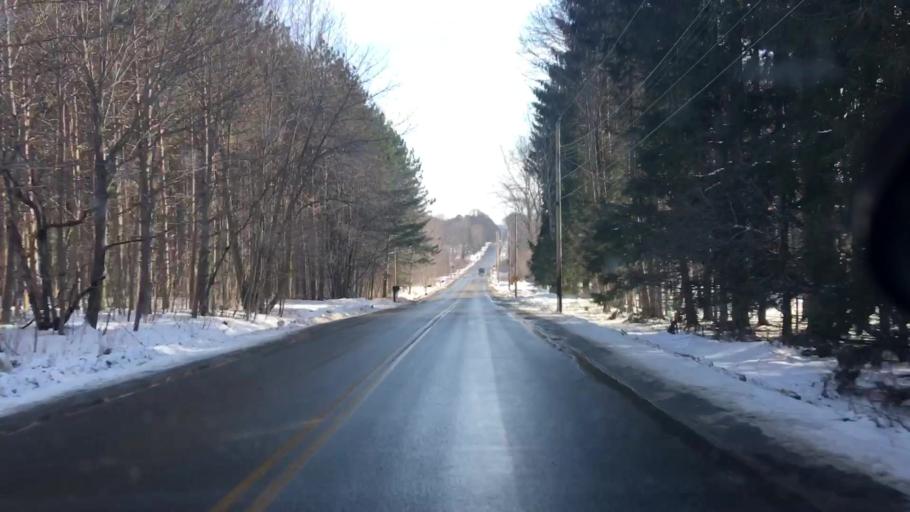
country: US
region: Maine
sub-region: Penobscot County
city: Hermon
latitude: 44.8522
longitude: -68.8445
